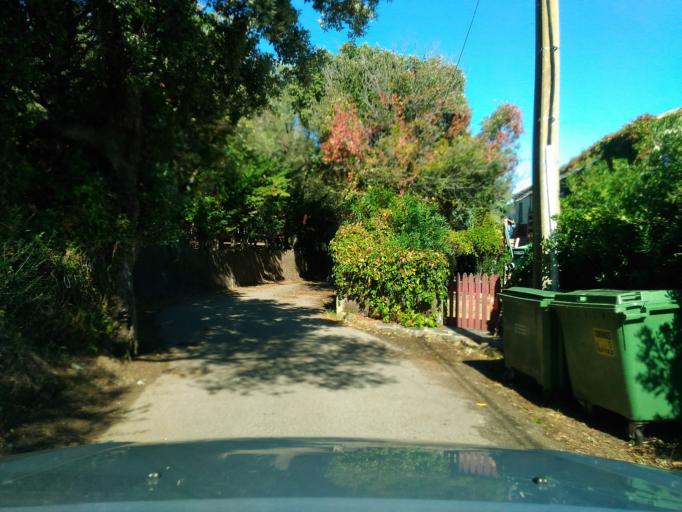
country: FR
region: Corsica
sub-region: Departement de la Haute-Corse
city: Brando
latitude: 42.9635
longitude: 9.4482
